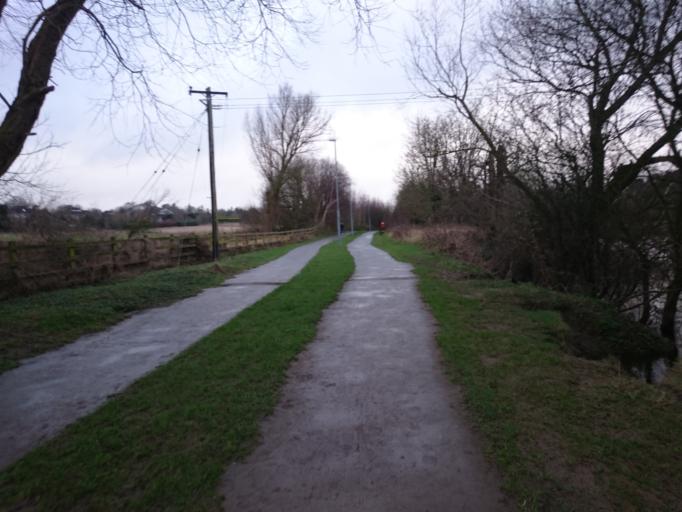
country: IE
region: Leinster
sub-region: Kilkenny
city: Kilkenny
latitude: 52.6699
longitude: -7.2623
